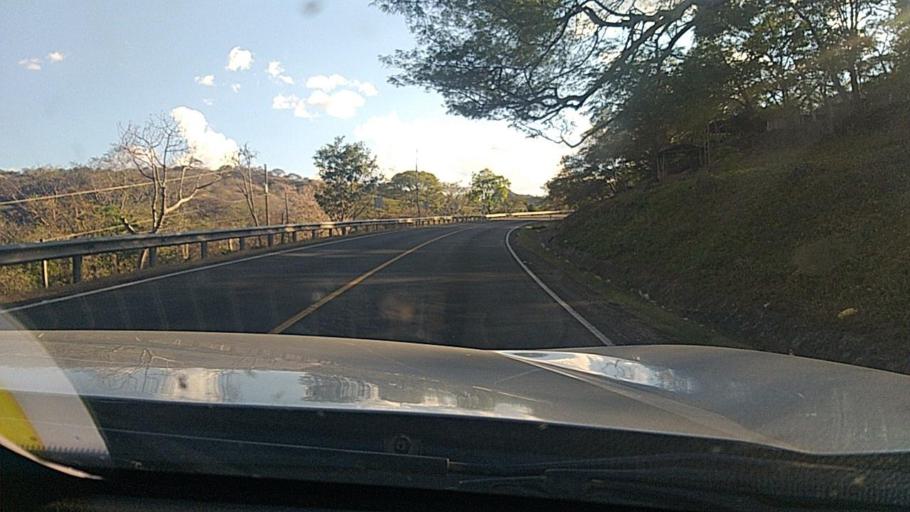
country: NI
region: Esteli
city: Condega
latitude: 13.2831
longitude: -86.3453
